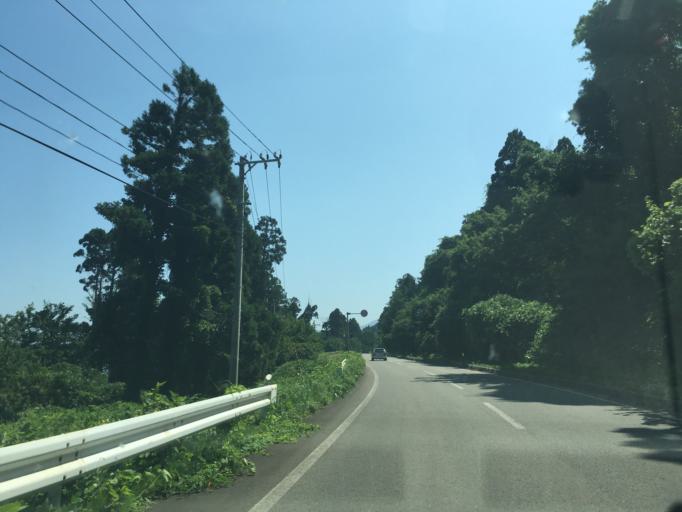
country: JP
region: Akita
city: Tenno
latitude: 39.9938
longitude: 139.7120
